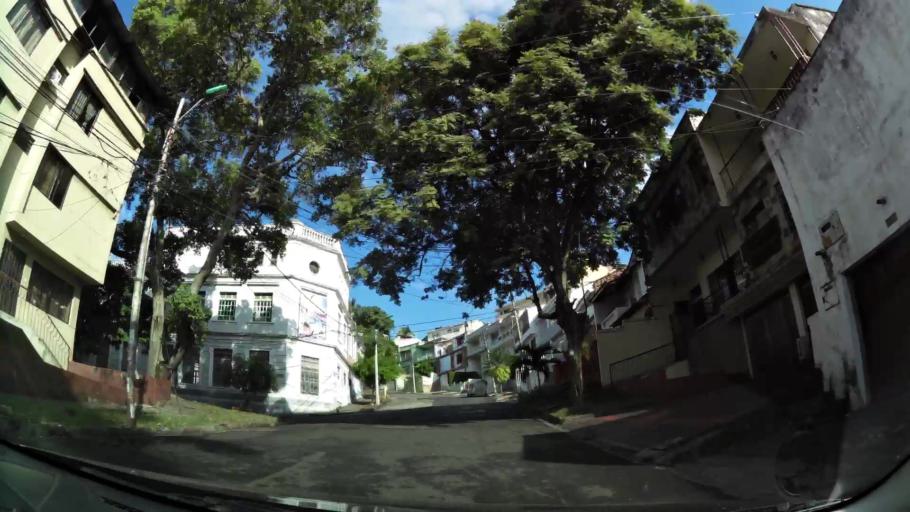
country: CO
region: Valle del Cauca
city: Cali
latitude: 3.4378
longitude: -76.5416
